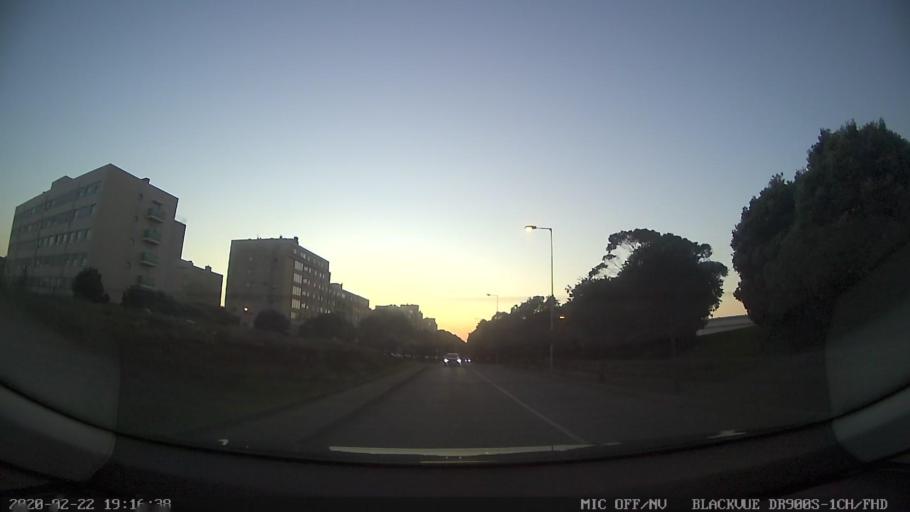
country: PT
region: Porto
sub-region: Matosinhos
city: Leca da Palmeira
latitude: 41.2011
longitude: -8.7029
